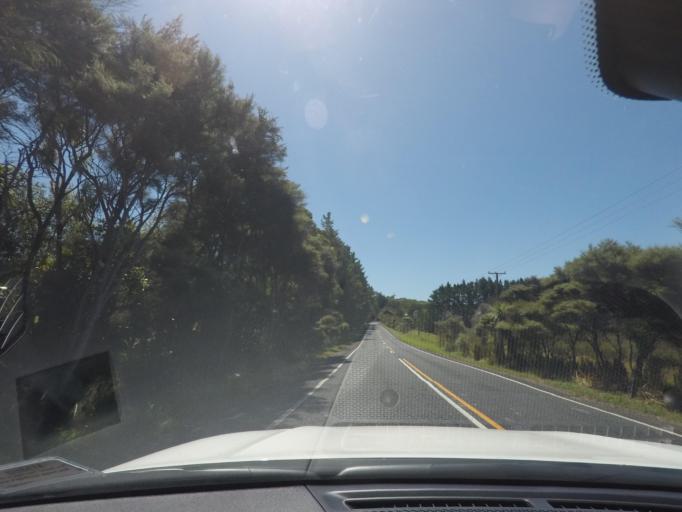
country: NZ
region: Auckland
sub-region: Auckland
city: Parakai
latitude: -36.6187
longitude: 174.3452
